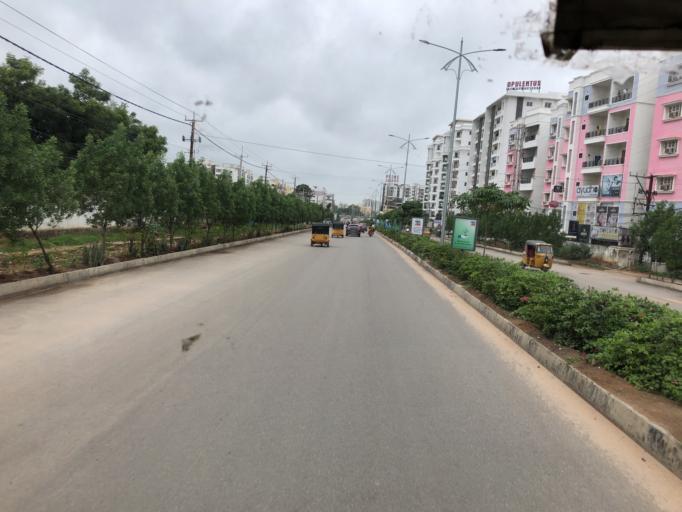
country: IN
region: Telangana
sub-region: Medak
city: Serilingampalle
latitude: 17.4620
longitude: 78.3511
